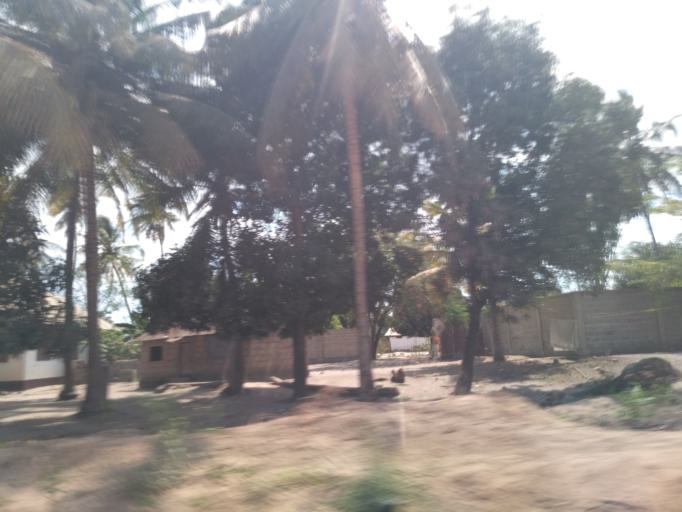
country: TZ
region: Dar es Salaam
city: Dar es Salaam
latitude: -6.8972
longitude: 39.3423
